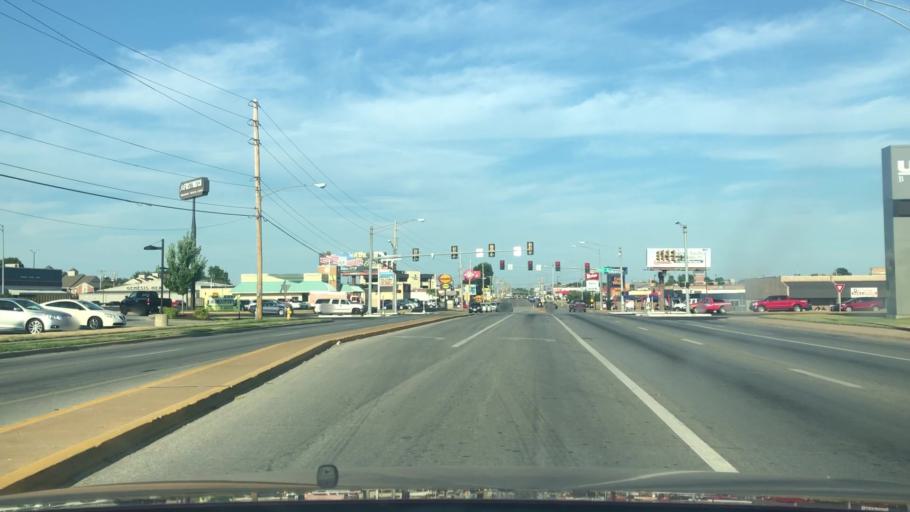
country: US
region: Missouri
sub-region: Greene County
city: Springfield
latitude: 37.1597
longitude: -93.2784
